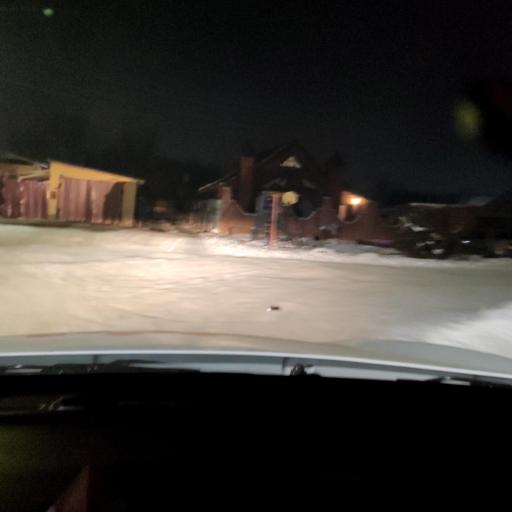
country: RU
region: Tatarstan
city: Stolbishchi
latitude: 55.6500
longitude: 49.2065
